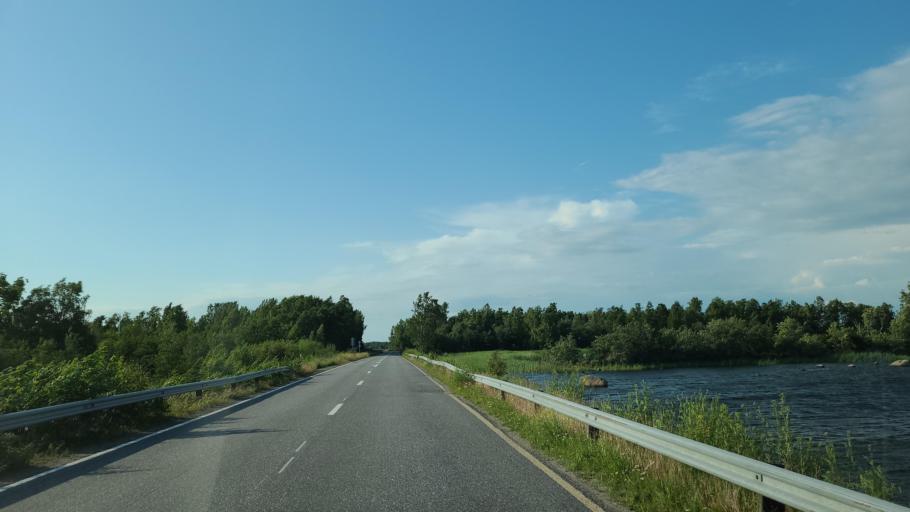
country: FI
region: Ostrobothnia
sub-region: Vaasa
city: Replot
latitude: 63.2769
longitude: 21.3424
